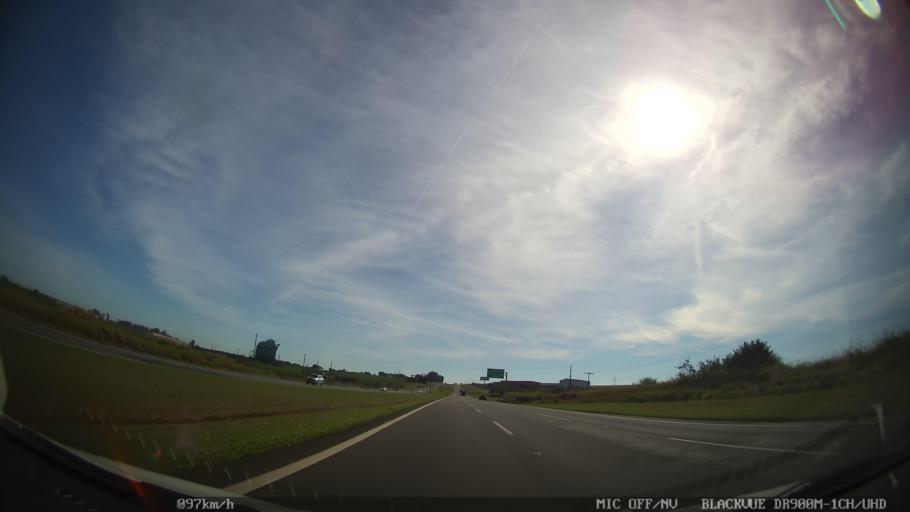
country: BR
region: Sao Paulo
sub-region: Cordeiropolis
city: Cordeiropolis
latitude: -22.4718
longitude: -47.3990
